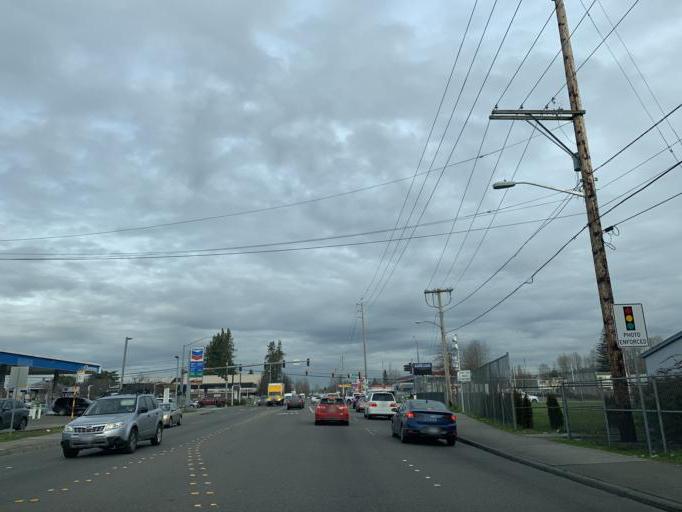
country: US
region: Washington
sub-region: King County
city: Kent
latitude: 47.3858
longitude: -122.2311
